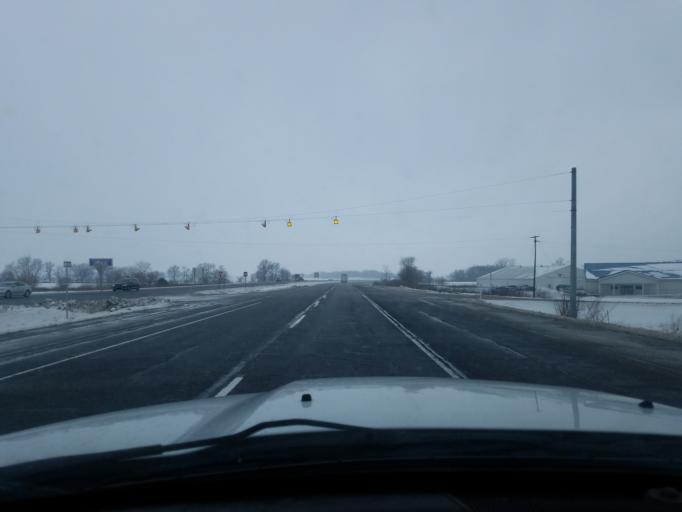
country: US
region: Indiana
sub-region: Fulton County
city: Rochester
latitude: 41.0484
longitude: -86.2301
